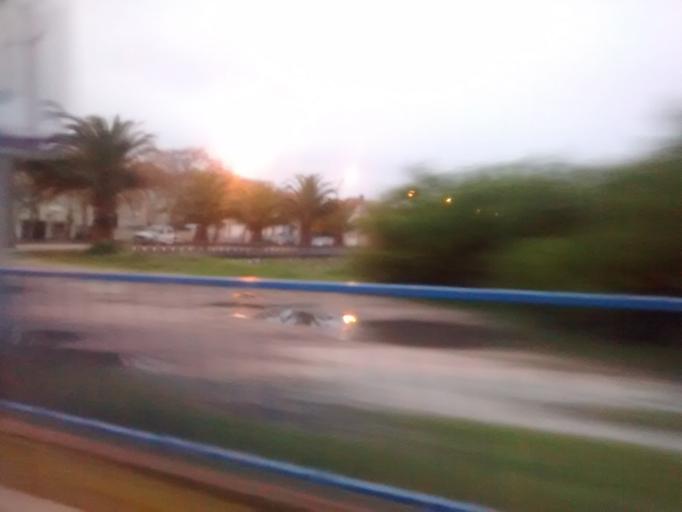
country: PT
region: Aveiro
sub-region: Aveiro
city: Aveiro
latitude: 40.6381
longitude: -8.6589
